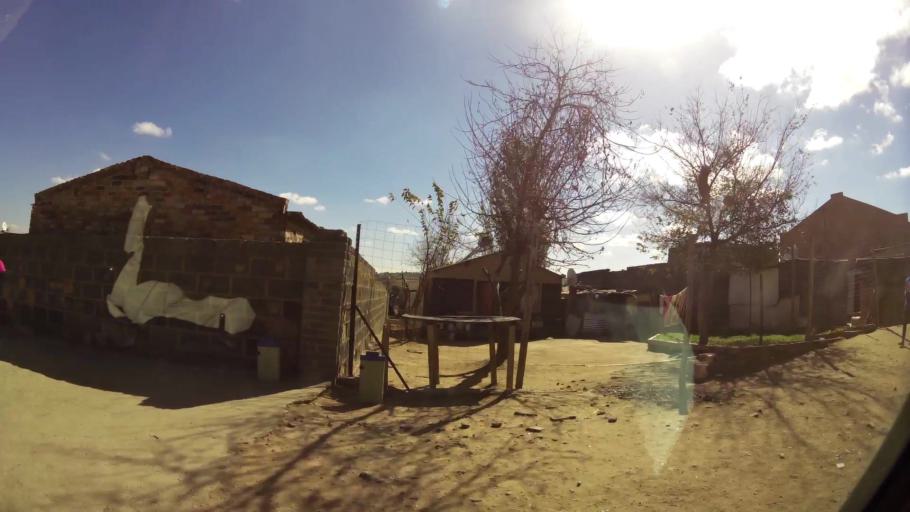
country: ZA
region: Gauteng
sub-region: City of Johannesburg Metropolitan Municipality
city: Midrand
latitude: -26.0302
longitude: 28.1639
